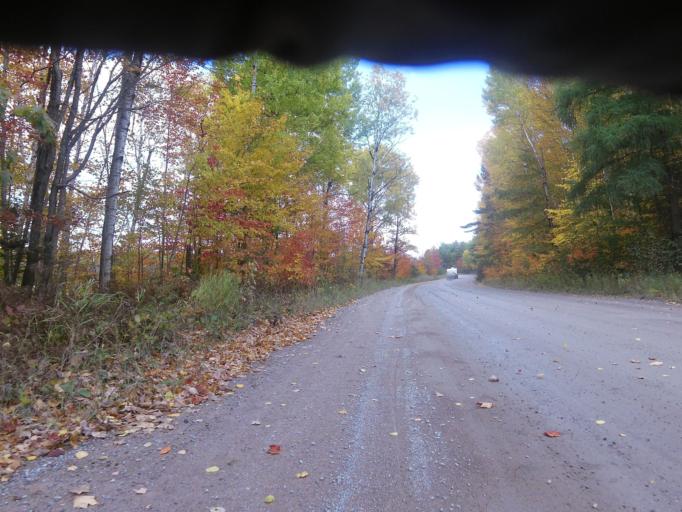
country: CA
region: Ontario
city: Petawawa
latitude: 45.8185
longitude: -77.4043
